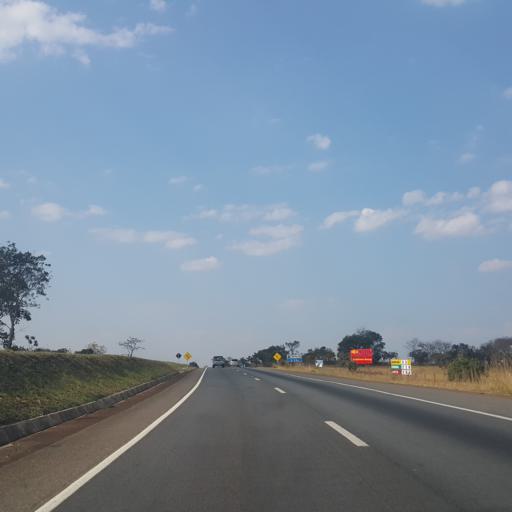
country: BR
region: Goias
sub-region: Abadiania
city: Abadiania
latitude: -16.1130
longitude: -48.5316
